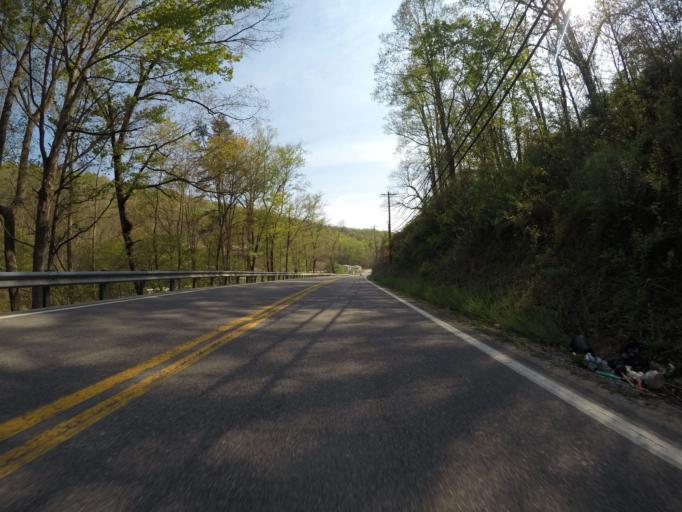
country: US
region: West Virginia
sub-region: Kanawha County
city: Coal Fork
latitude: 38.3826
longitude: -81.5612
